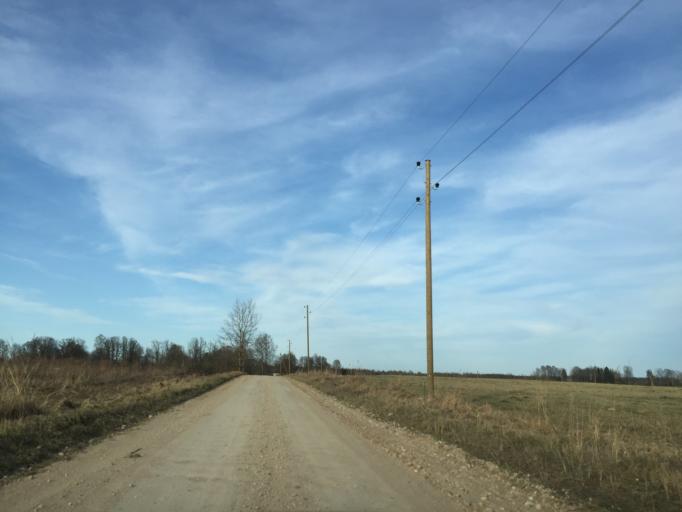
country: LV
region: Kegums
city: Kegums
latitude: 56.8033
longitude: 24.7743
